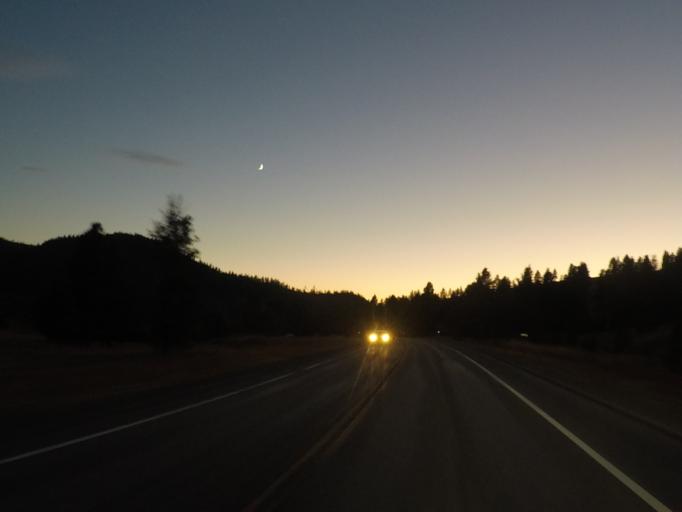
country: US
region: Montana
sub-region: Missoula County
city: Seeley Lake
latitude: 47.0288
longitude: -113.2834
